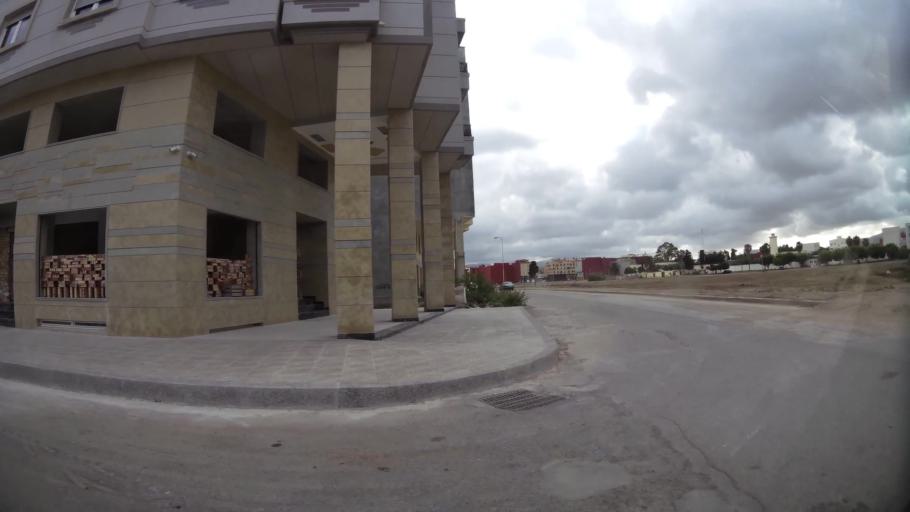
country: MA
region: Oriental
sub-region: Nador
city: Nador
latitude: 35.1568
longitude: -2.9231
